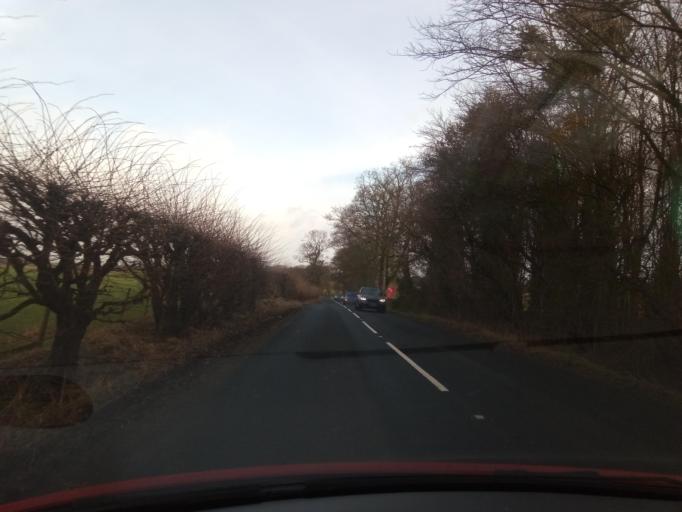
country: GB
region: England
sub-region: Northumberland
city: Acomb
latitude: 55.0854
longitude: -2.0686
